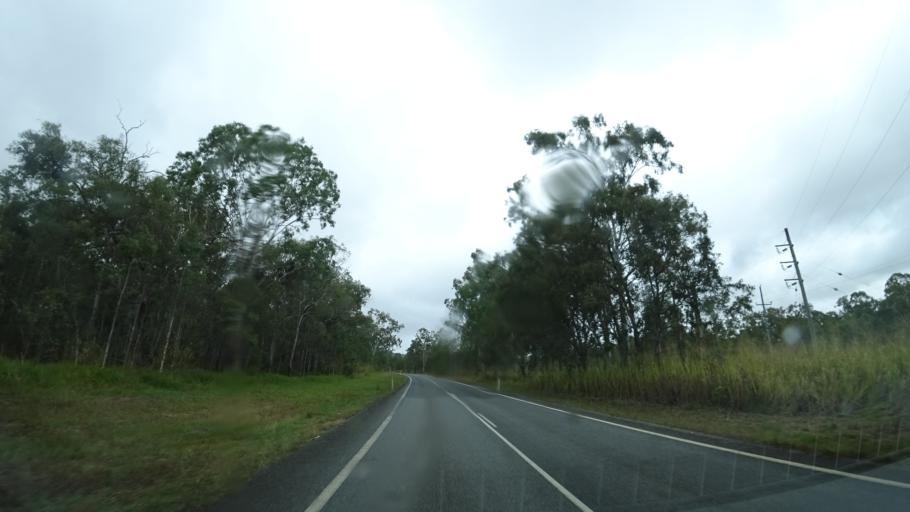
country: AU
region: Queensland
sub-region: Cairns
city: Port Douglas
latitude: -16.6923
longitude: 145.3375
